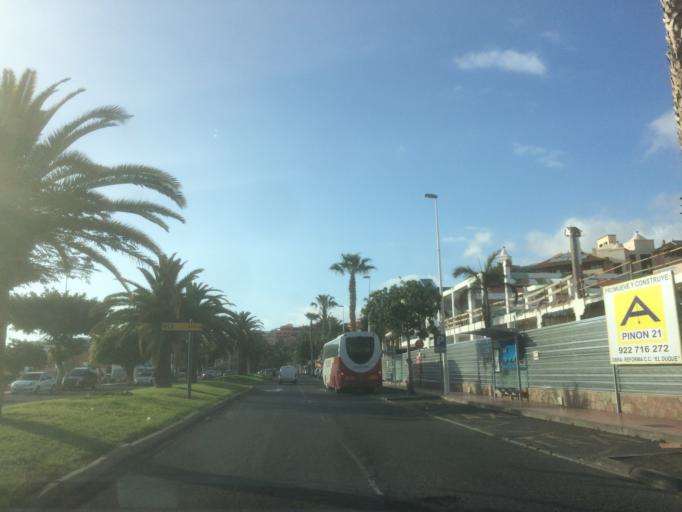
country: ES
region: Canary Islands
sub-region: Provincia de Santa Cruz de Tenerife
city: Playa de las Americas
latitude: 28.0918
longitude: -16.7357
